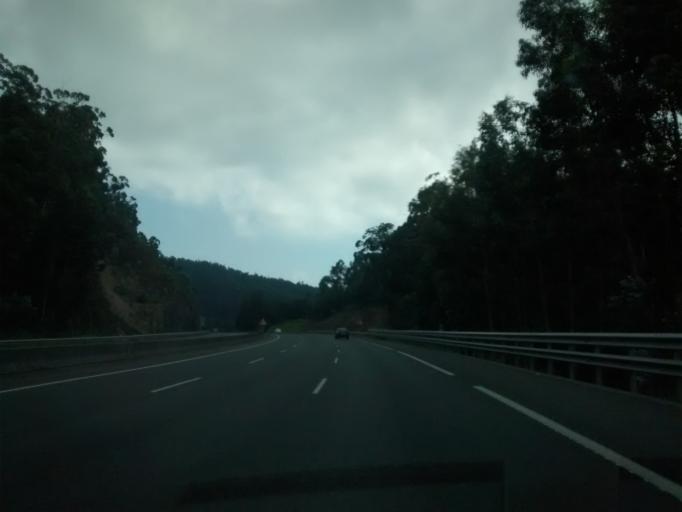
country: ES
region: Galicia
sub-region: Provincia de Pontevedra
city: Meis
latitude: 42.4809
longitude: -8.7710
